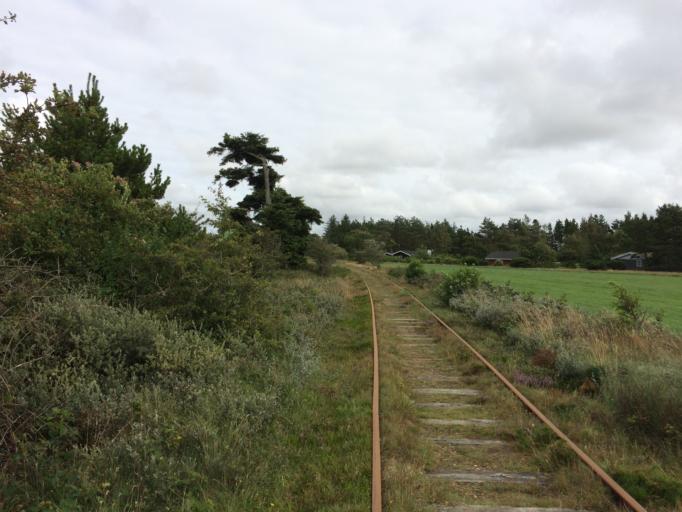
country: DK
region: South Denmark
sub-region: Varde Kommune
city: Oksbol
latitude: 55.7874
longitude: 8.2361
